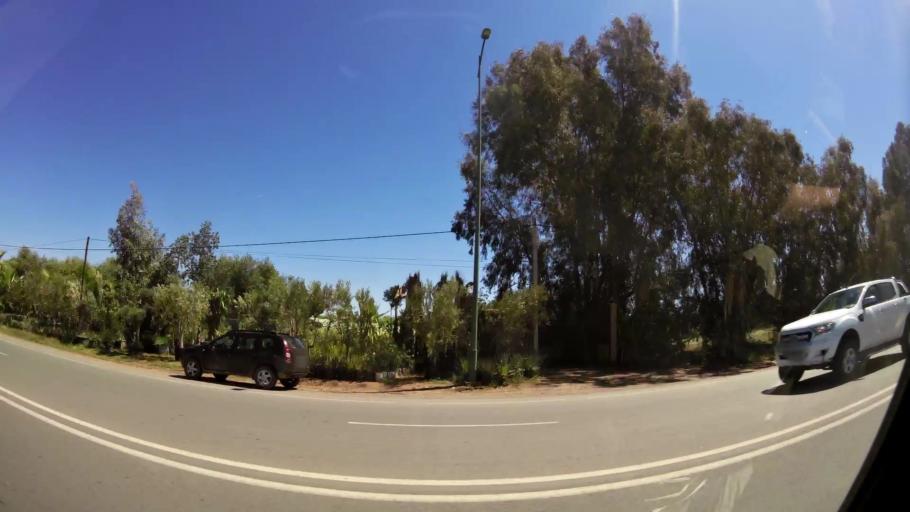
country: MA
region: Marrakech-Tensift-Al Haouz
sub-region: Marrakech
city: Marrakesh
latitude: 31.5657
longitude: -7.9804
